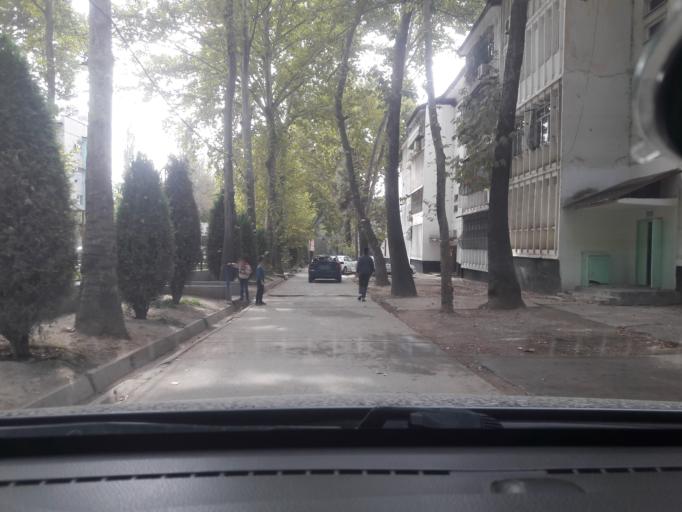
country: TJ
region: Dushanbe
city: Dushanbe
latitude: 38.5881
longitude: 68.7500
